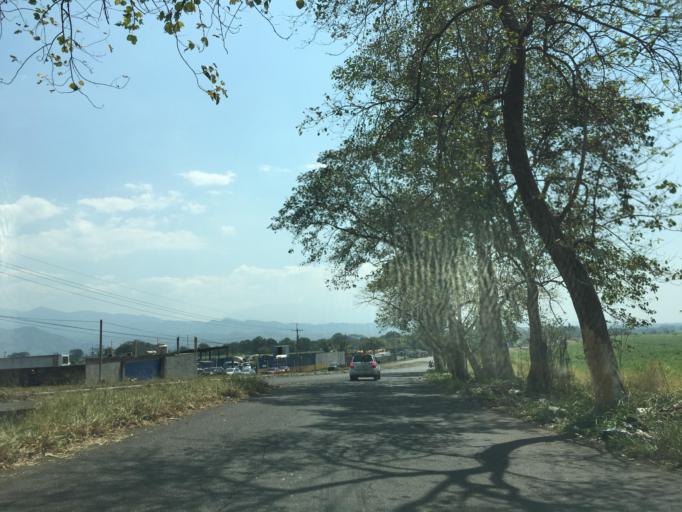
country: GT
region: Escuintla
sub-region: Municipio de Escuintla
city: Escuintla
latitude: 14.2772
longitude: -90.7629
